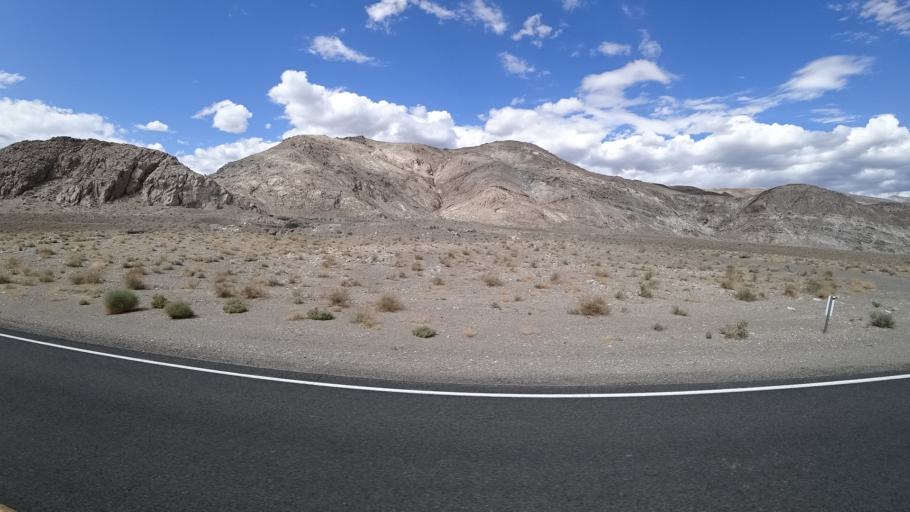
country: US
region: California
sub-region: Inyo County
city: Lone Pine
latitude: 36.5344
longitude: -117.9222
